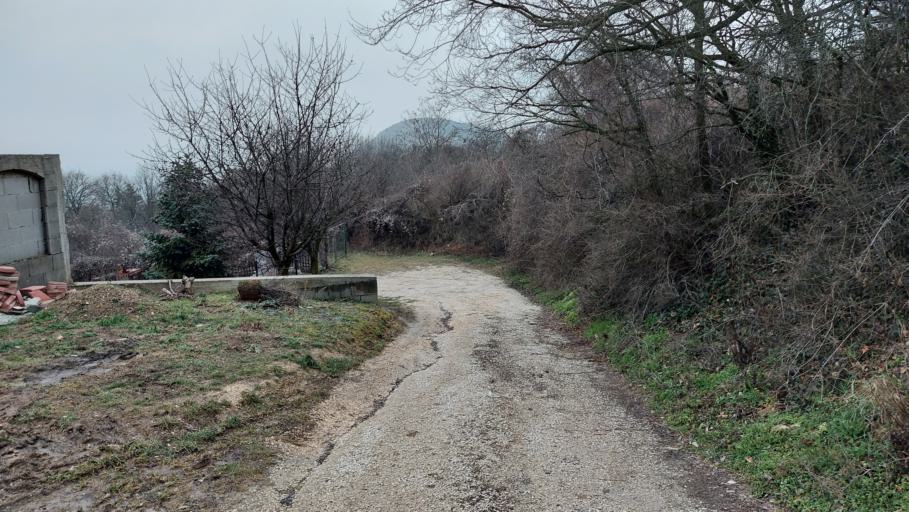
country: HU
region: Pest
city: Budaors
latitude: 47.4714
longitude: 18.9589
